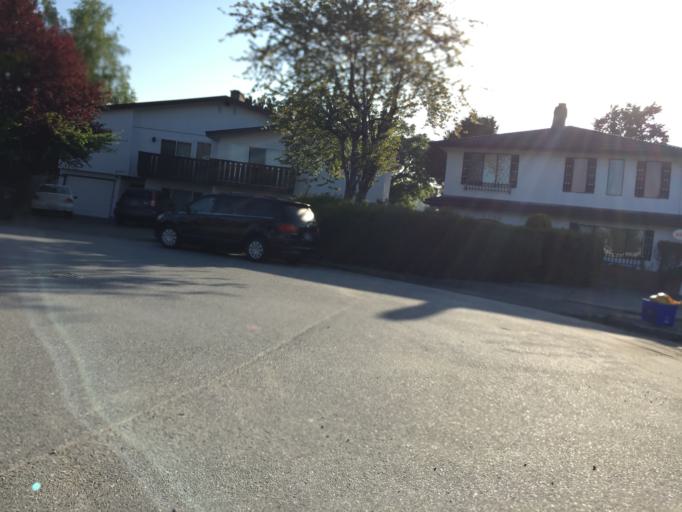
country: CA
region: British Columbia
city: Richmond
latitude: 49.1451
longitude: -123.1271
